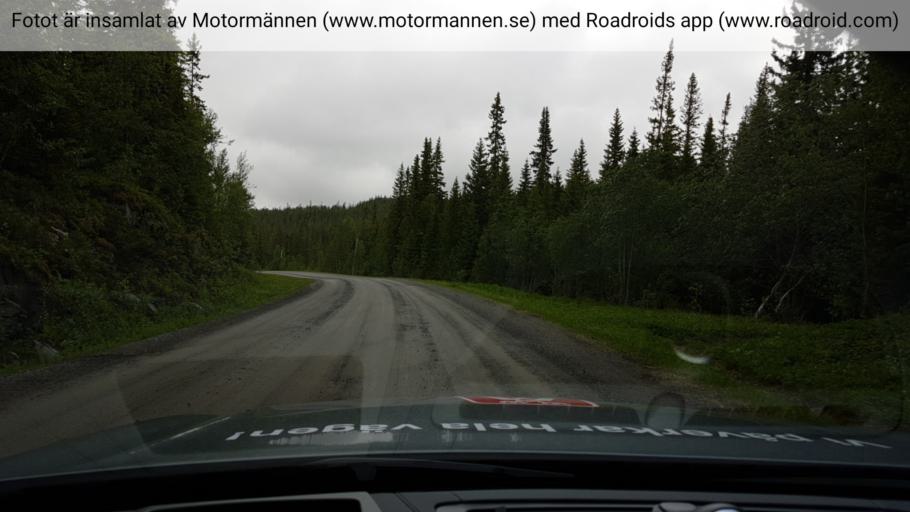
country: SE
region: Jaemtland
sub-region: Are Kommun
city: Are
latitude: 63.7216
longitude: 12.6074
